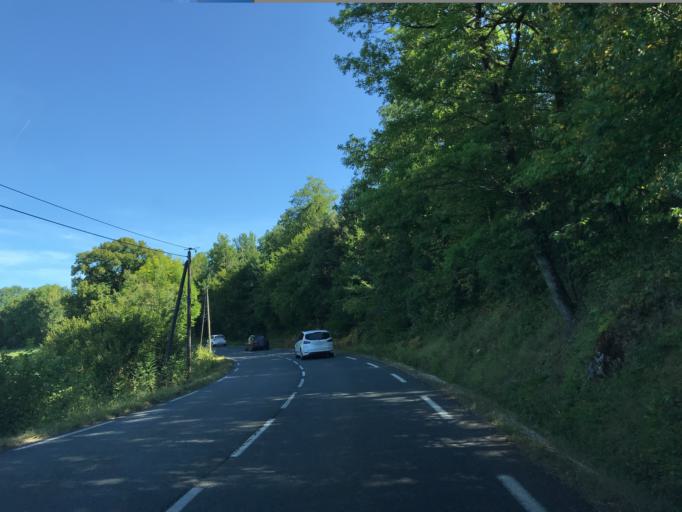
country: FR
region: Limousin
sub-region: Departement de la Correze
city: Larche
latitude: 45.0842
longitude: 1.3743
